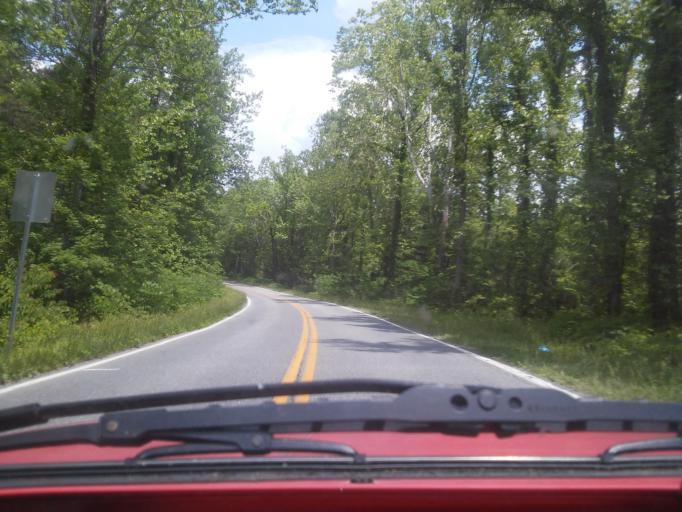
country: US
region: Virginia
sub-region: Craig County
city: New Castle
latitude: 37.5616
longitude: -80.0421
